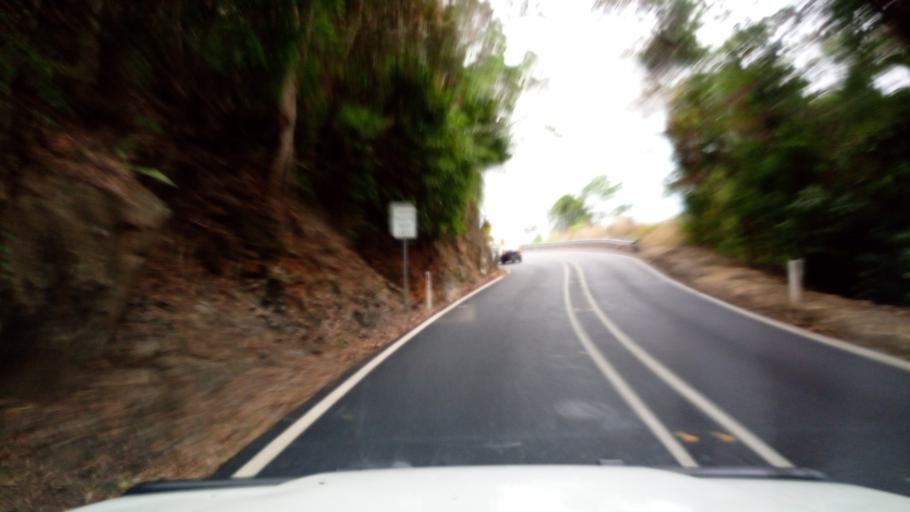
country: AU
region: Queensland
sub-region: Tablelands
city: Kuranda
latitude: -16.8389
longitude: 145.6719
